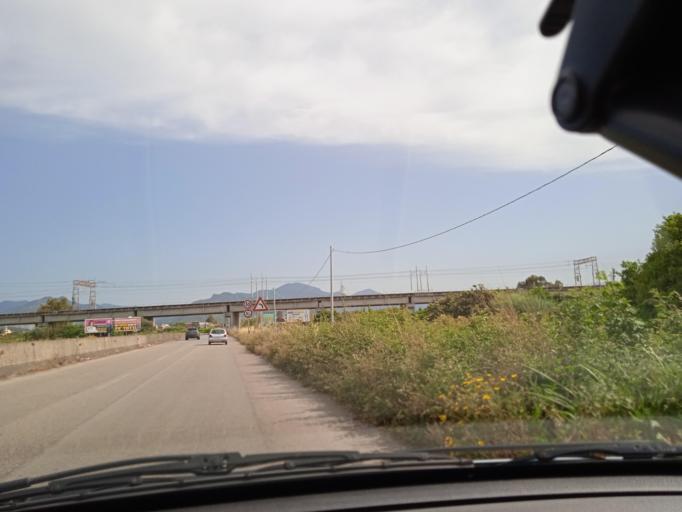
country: IT
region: Sicily
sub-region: Messina
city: Milazzo
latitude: 38.2008
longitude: 15.2467
